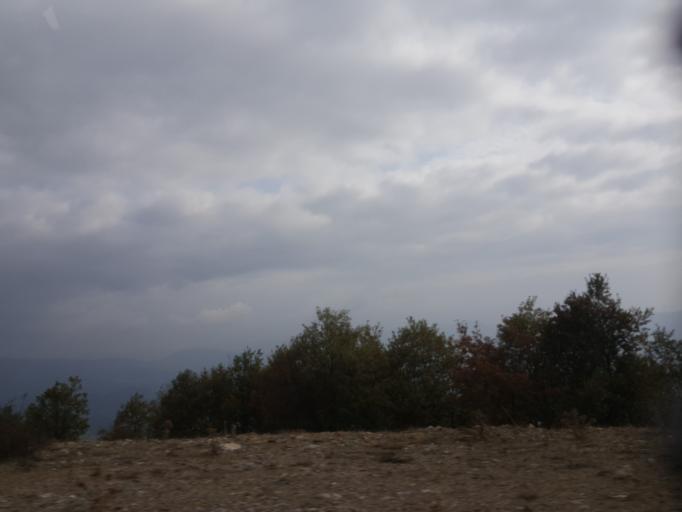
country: TR
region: Sinop
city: Duragan
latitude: 41.4922
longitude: 35.0349
